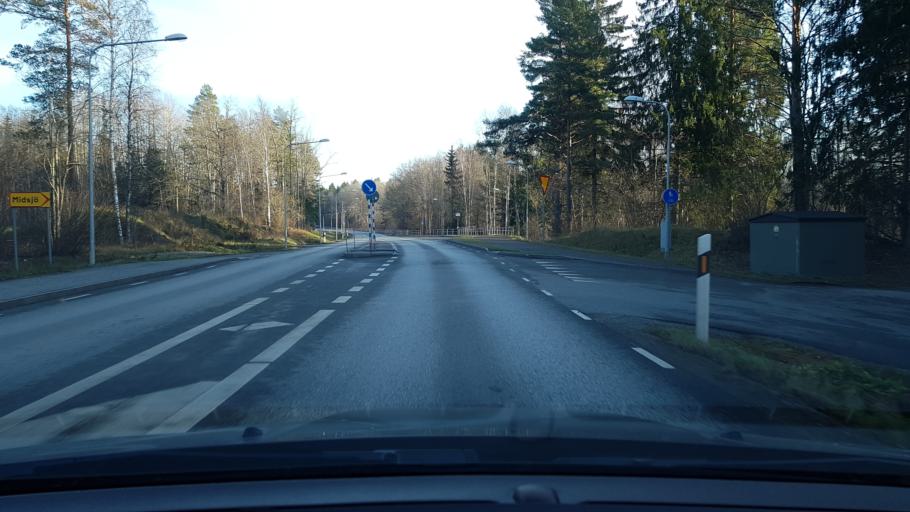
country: SE
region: Stockholm
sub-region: Norrtalje Kommun
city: Rimbo
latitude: 59.7397
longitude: 18.3312
